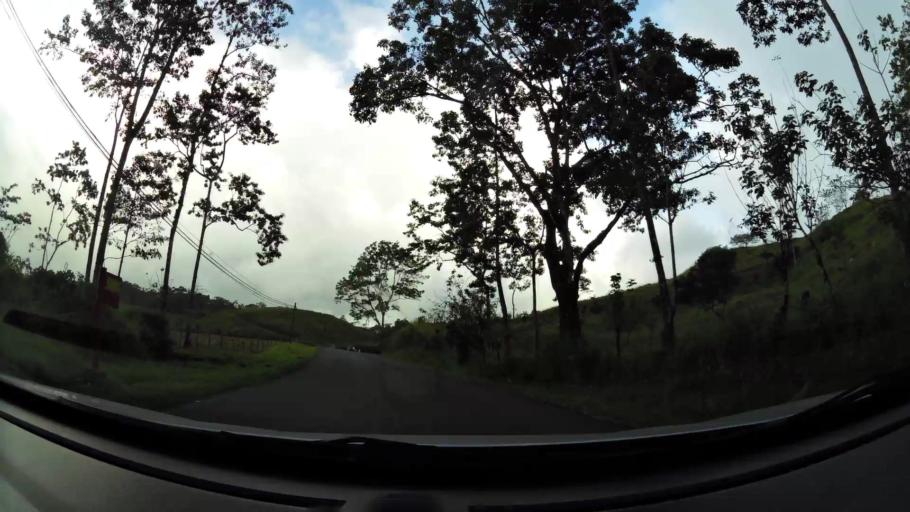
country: CR
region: Cartago
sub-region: Canton de Turrialba
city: La Suiza
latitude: 9.9677
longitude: -83.5701
